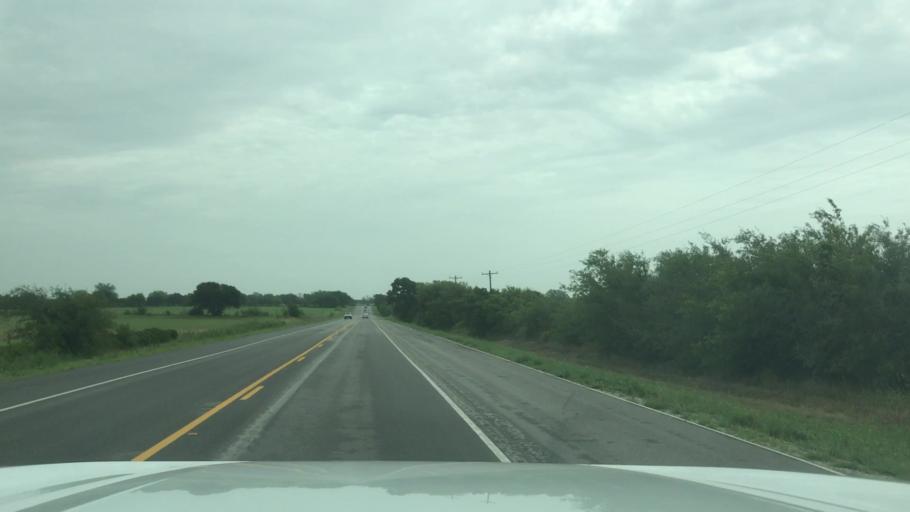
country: US
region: Texas
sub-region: Eastland County
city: Gorman
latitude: 32.2219
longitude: -98.6945
